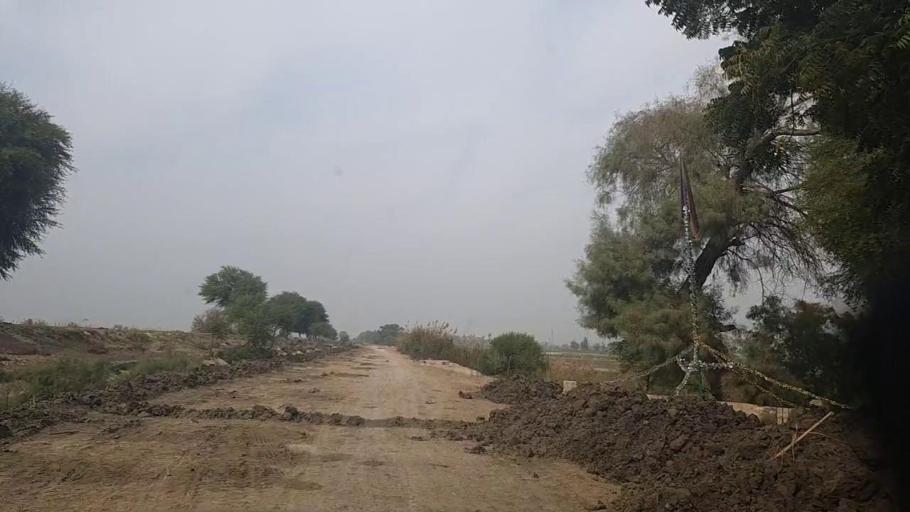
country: PK
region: Sindh
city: Daur
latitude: 26.3151
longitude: 68.2035
